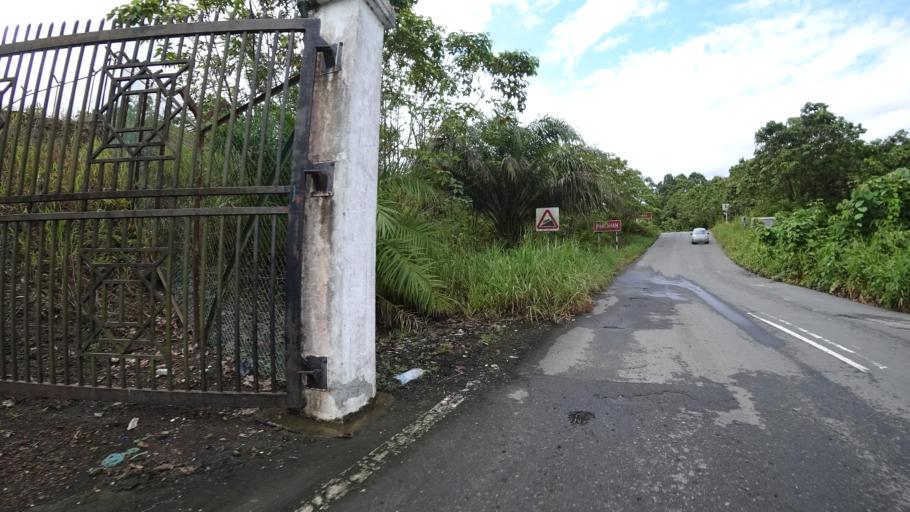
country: BN
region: Temburong
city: Bangar
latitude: 4.7924
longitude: 115.2365
